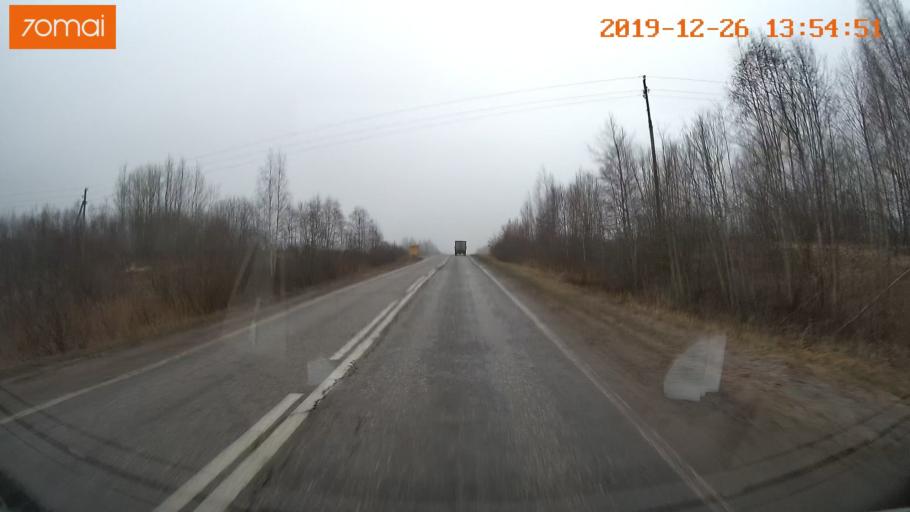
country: RU
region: Jaroslavl
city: Poshekhon'ye
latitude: 58.6093
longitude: 38.6403
